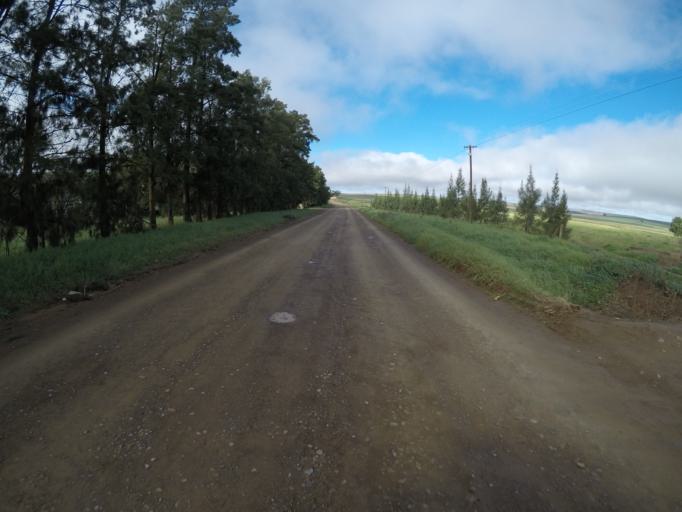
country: ZA
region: Western Cape
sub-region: Cape Winelands District Municipality
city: Ashton
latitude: -34.1427
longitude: 19.8646
